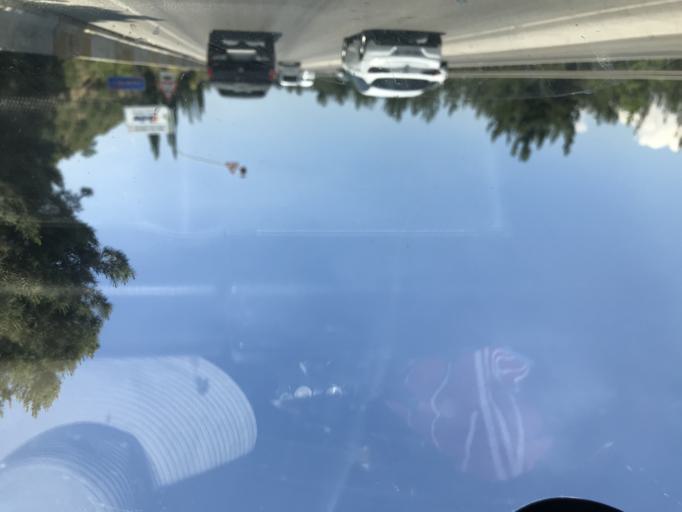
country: TR
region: Denizli
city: Denizli
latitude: 37.7314
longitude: 29.1731
